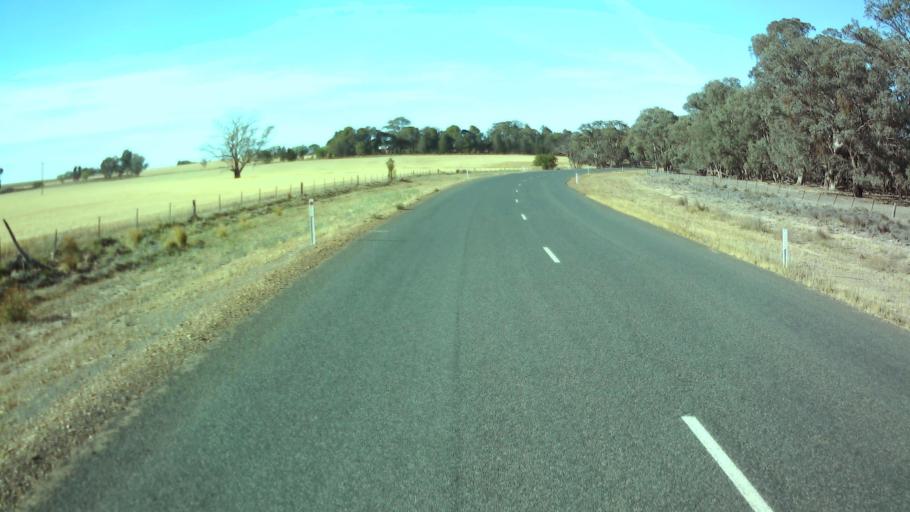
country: AU
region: New South Wales
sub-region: Weddin
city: Grenfell
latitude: -33.9866
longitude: 148.1406
